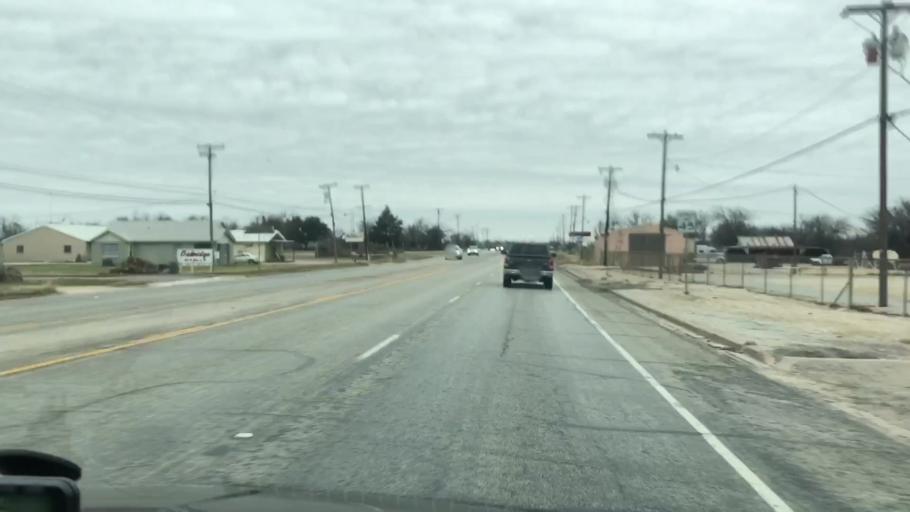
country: US
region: Texas
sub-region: Jack County
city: Jacksboro
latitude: 33.2062
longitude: -98.1540
